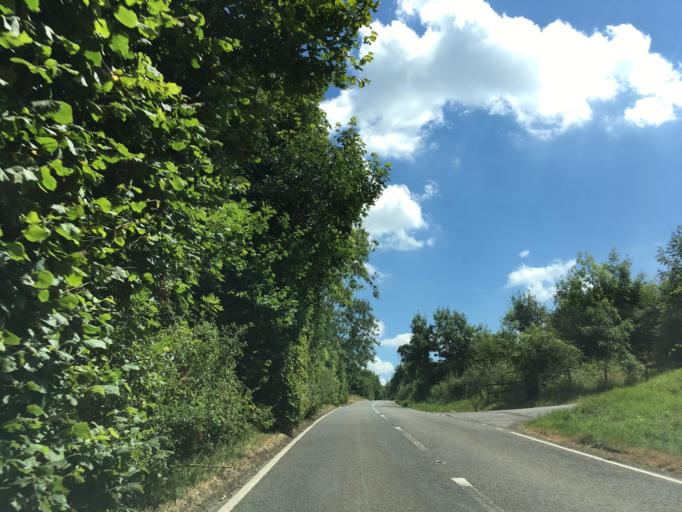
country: GB
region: England
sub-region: Gloucestershire
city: Painswick
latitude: 51.8118
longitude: -2.2025
